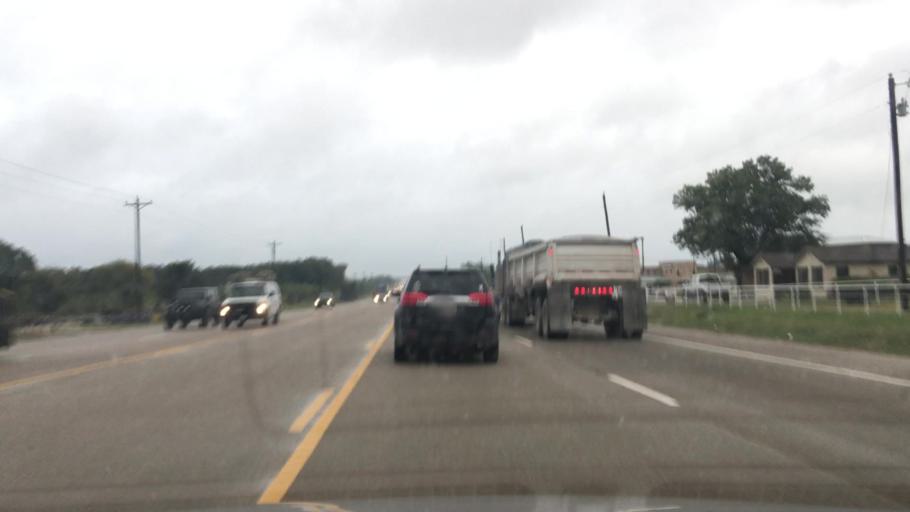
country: US
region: Texas
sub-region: Denton County
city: Cross Roads
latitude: 33.2275
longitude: -96.9934
